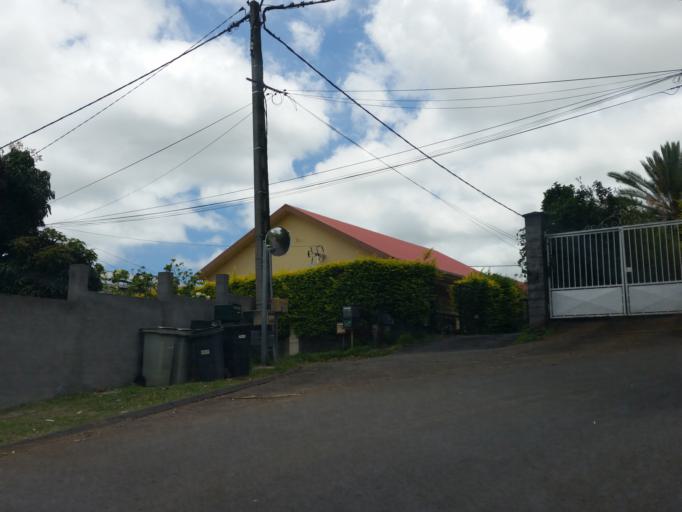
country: RE
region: Reunion
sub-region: Reunion
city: Sainte-Marie
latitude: -20.9329
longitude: 55.5418
